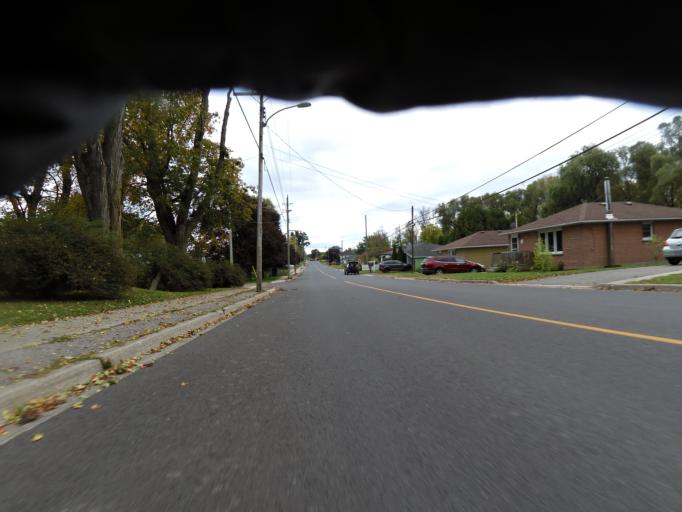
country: CA
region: Ontario
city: Cobourg
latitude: 44.0029
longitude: -77.8871
